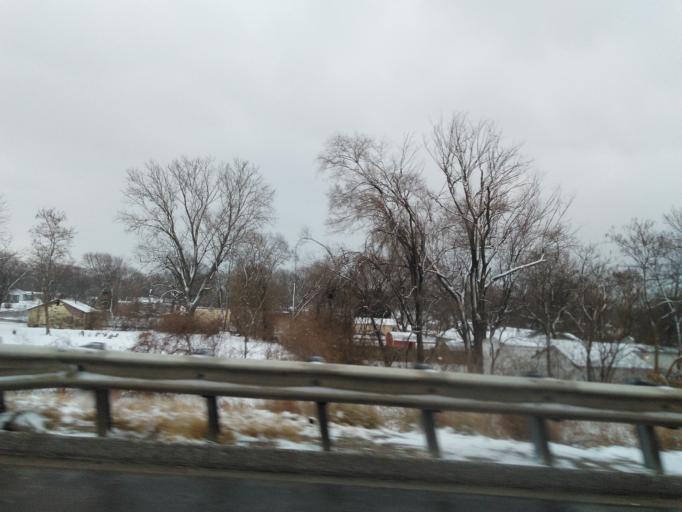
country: US
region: Illinois
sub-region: Saint Clair County
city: Cahokia
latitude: 38.5549
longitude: -90.1556
